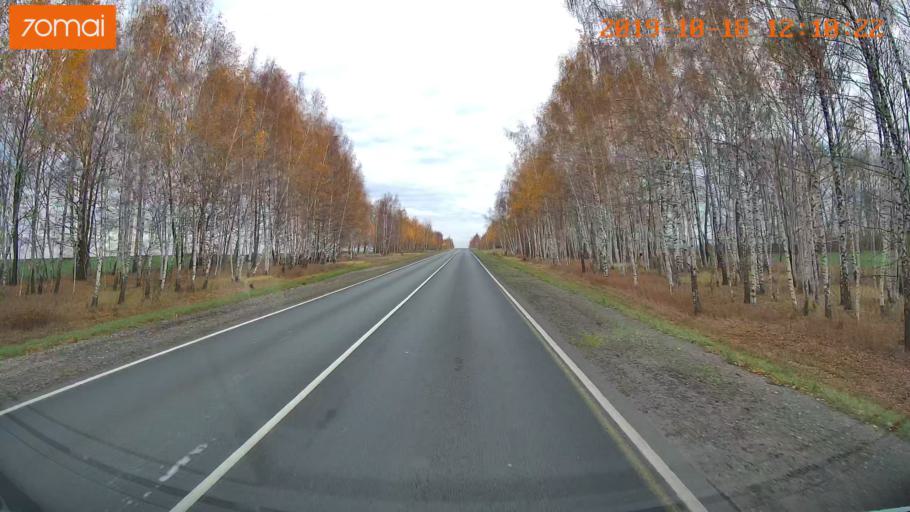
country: RU
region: Rjazan
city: Zakharovo
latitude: 54.3917
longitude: 39.3293
